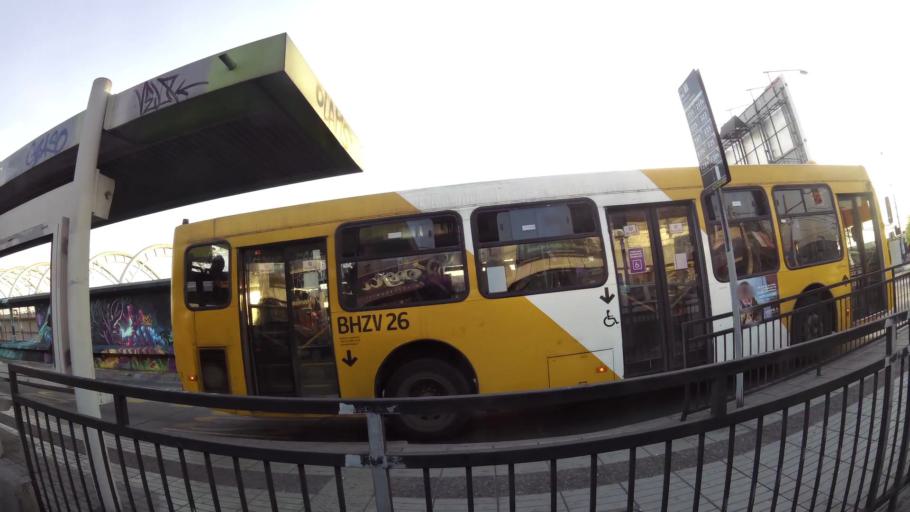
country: CL
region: Santiago Metropolitan
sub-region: Provincia de Santiago
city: La Pintana
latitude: -33.5306
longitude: -70.5950
